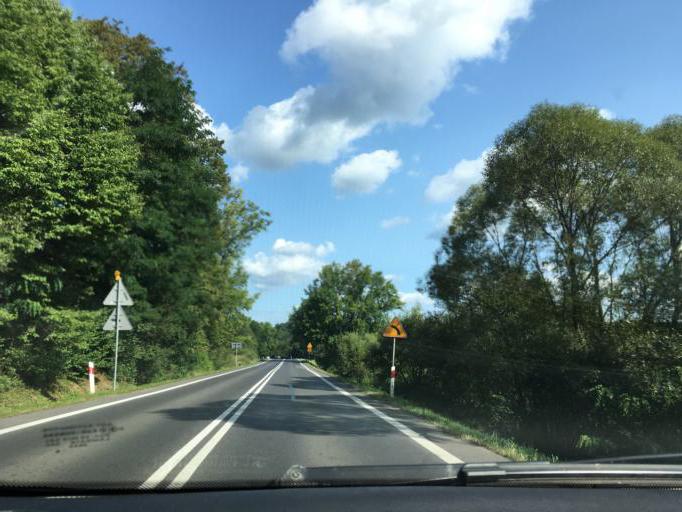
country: PL
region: Subcarpathian Voivodeship
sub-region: Powiat leski
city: Lesko
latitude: 49.4846
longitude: 22.3233
